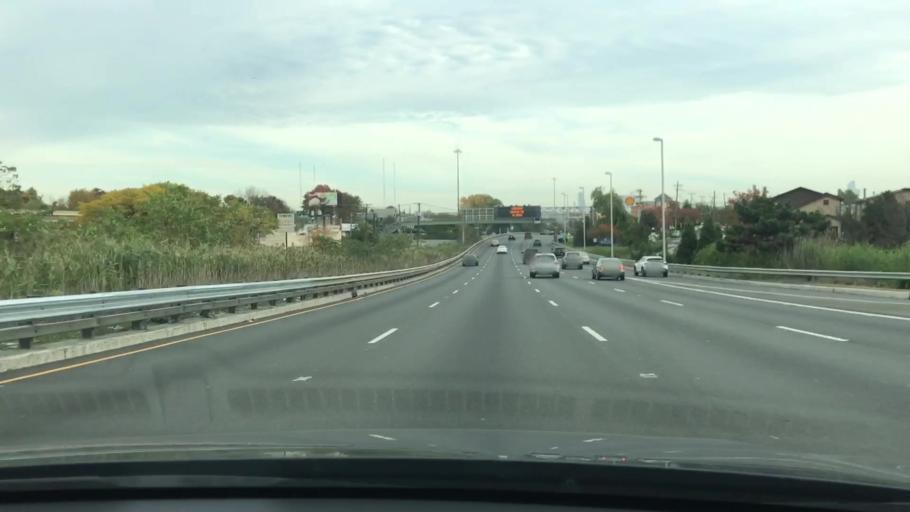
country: US
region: New Jersey
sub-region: Hudson County
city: Secaucus
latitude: 40.7970
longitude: -74.0648
